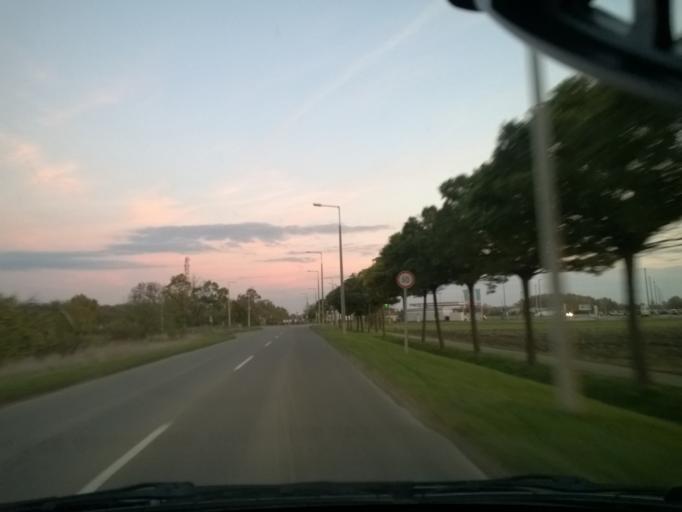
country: HU
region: Csongrad
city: Szentes
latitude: 46.6672
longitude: 20.2355
